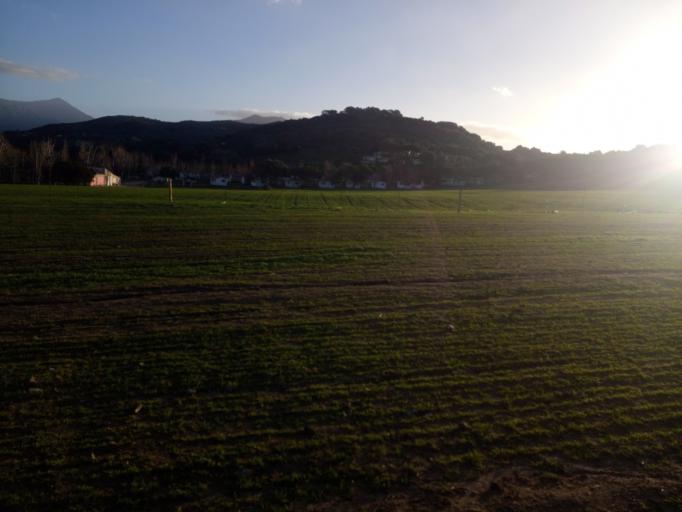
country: FR
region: Corsica
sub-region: Departement de la Corse-du-Sud
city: Appietto
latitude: 42.0712
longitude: 8.7271
